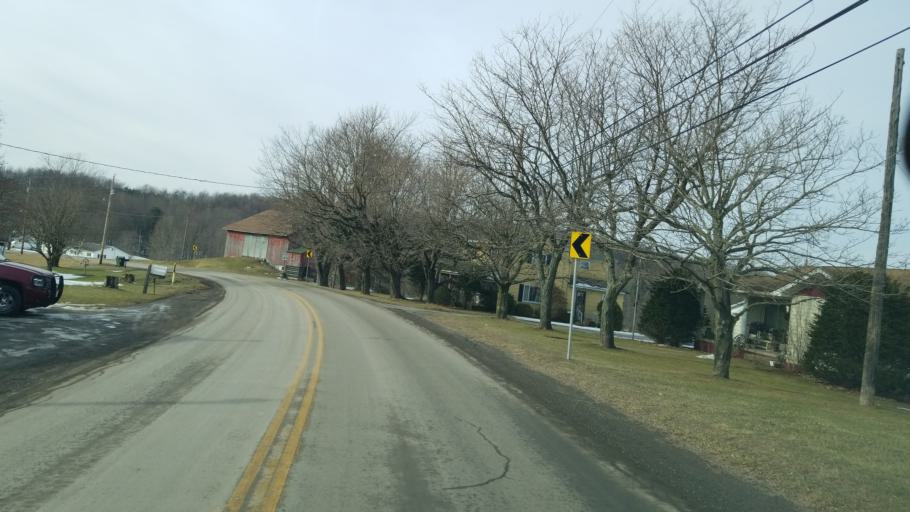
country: US
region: Pennsylvania
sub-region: Indiana County
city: Johnsonburg
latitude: 40.8398
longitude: -78.8615
